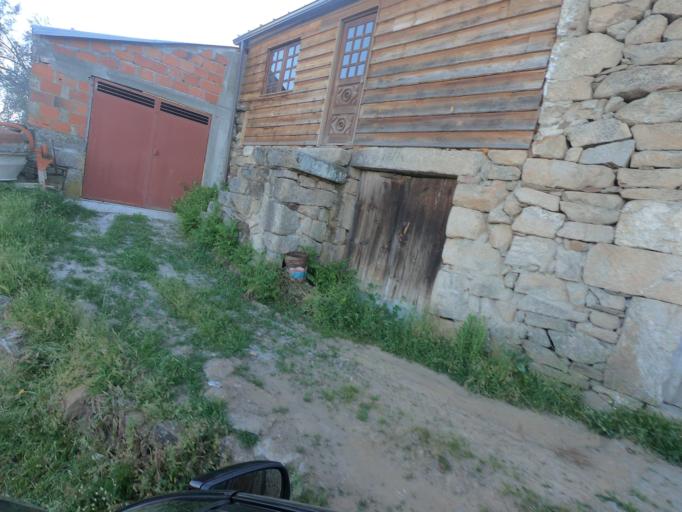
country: PT
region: Vila Real
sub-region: Vila Real
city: Vila Real
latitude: 41.3450
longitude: -7.7374
